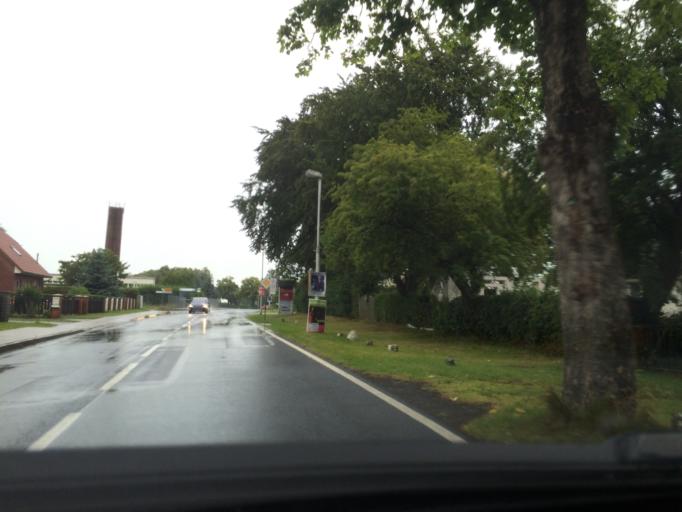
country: DE
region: Mecklenburg-Vorpommern
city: Prohn
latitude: 54.3757
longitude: 13.0232
